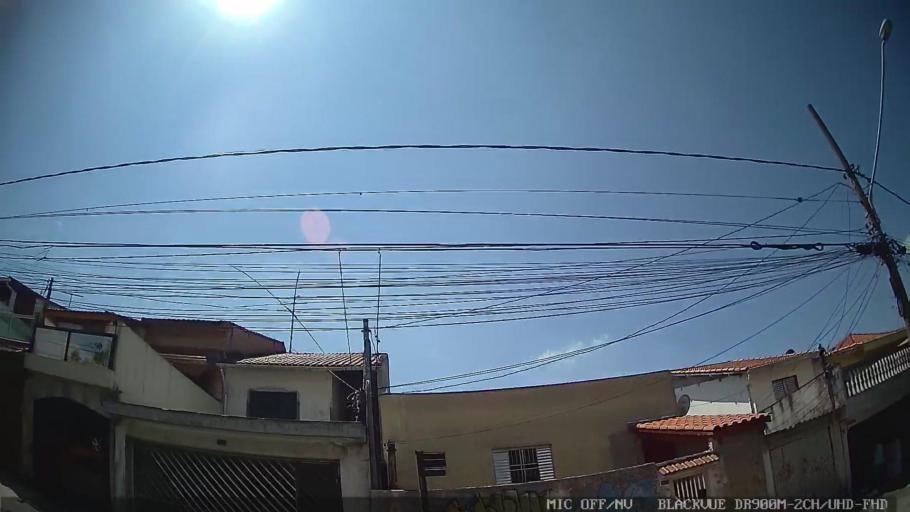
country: BR
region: Sao Paulo
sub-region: Guarulhos
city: Guarulhos
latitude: -23.5017
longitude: -46.5142
